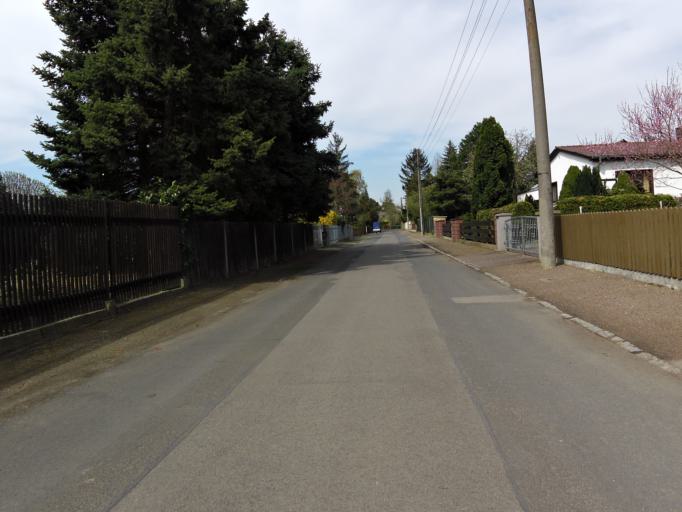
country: DE
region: Saxony
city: Markranstadt
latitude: 51.3146
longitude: 12.2758
